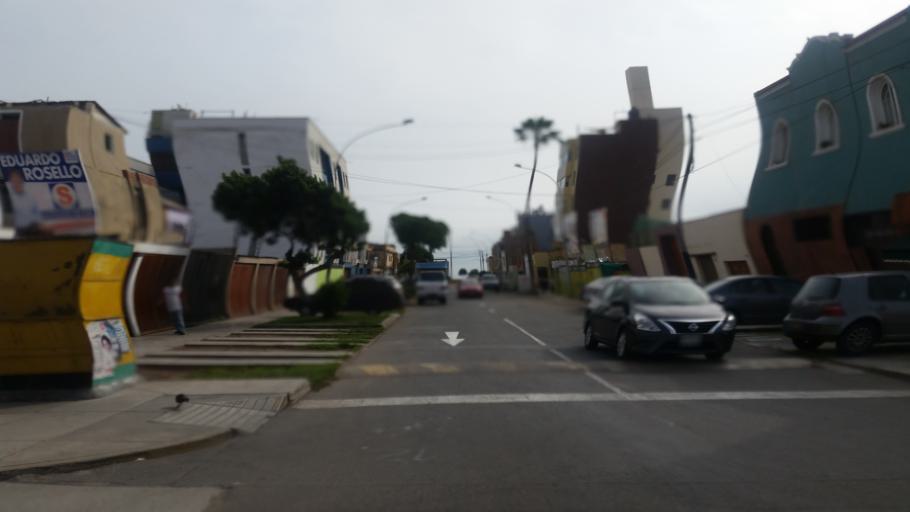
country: PE
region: Lima
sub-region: Lima
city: San Isidro
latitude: -12.0943
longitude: -77.0750
